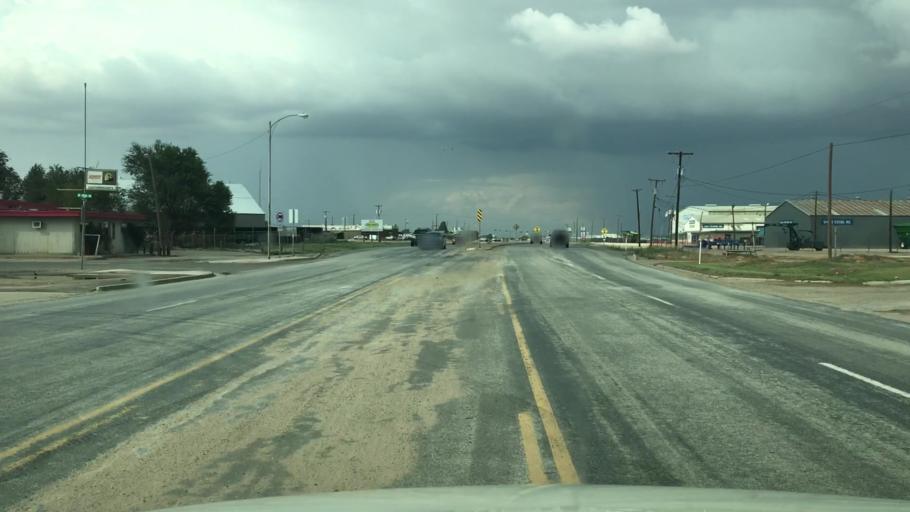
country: US
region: Texas
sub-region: Dawson County
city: Lamesa
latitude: 32.7510
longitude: -101.9509
